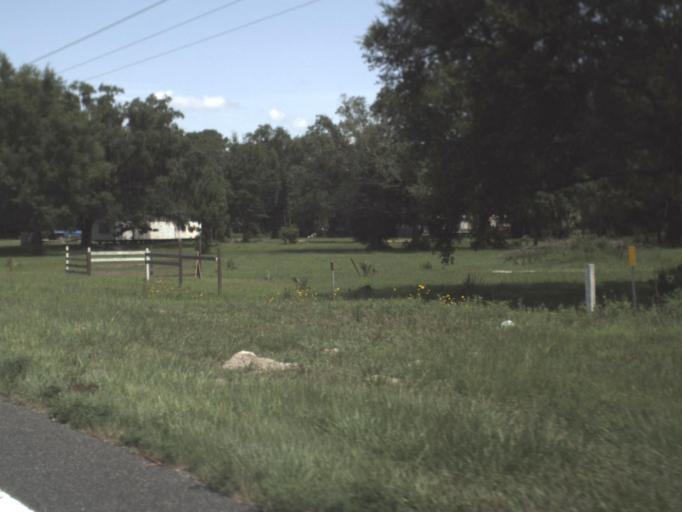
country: US
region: Florida
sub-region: Taylor County
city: Perry
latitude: 30.0218
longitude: -83.5339
